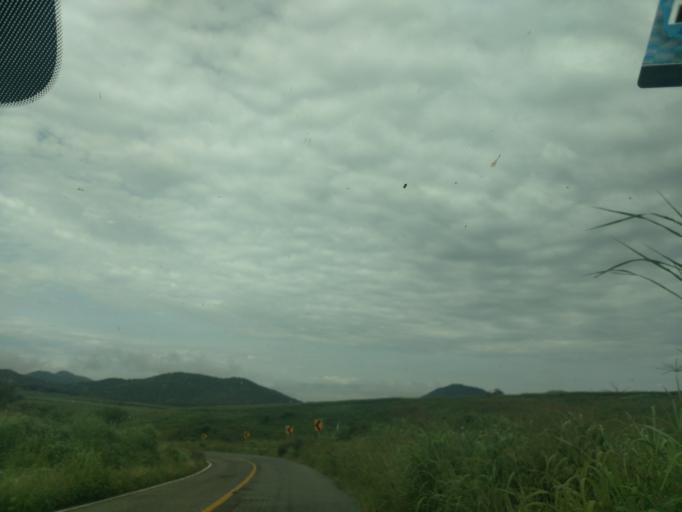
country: MX
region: Jalisco
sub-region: Atengo
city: Soyatlan del Oro
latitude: 20.5272
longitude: -104.3341
